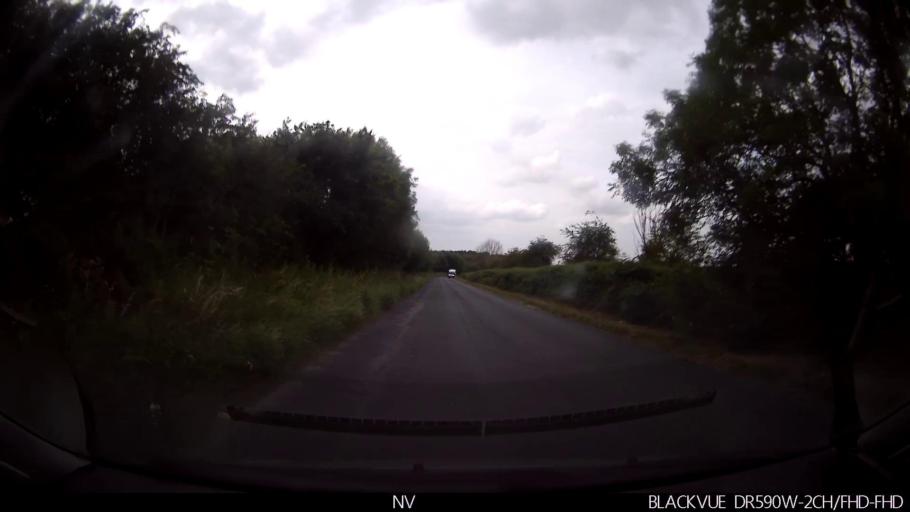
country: GB
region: England
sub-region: City of York
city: Holtby
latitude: 54.0418
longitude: -0.9568
